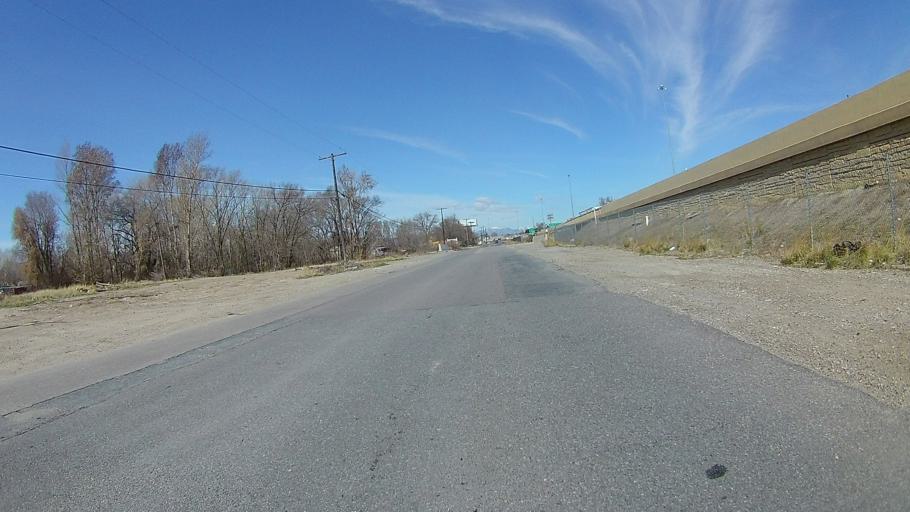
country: US
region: Utah
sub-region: Utah County
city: American Fork
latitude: 40.3676
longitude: -111.7972
